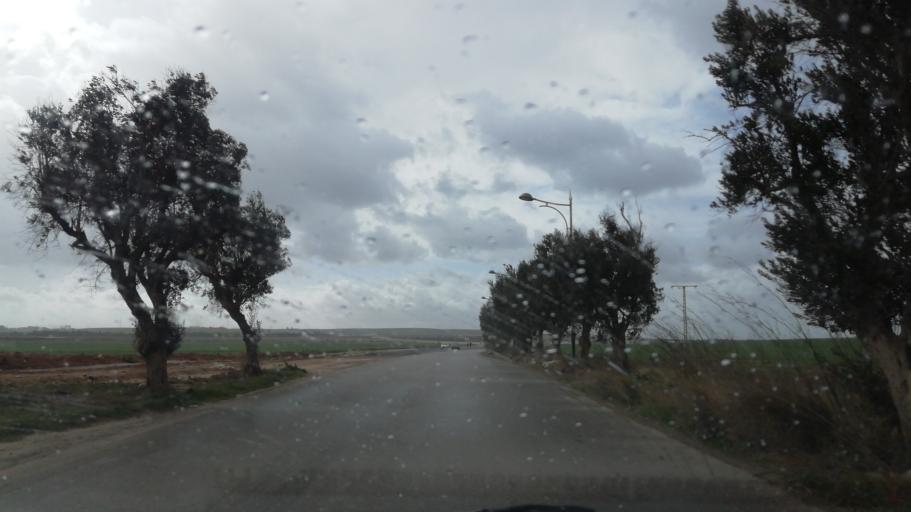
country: DZ
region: Oran
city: Sidi ech Chahmi
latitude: 35.6487
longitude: -0.5237
